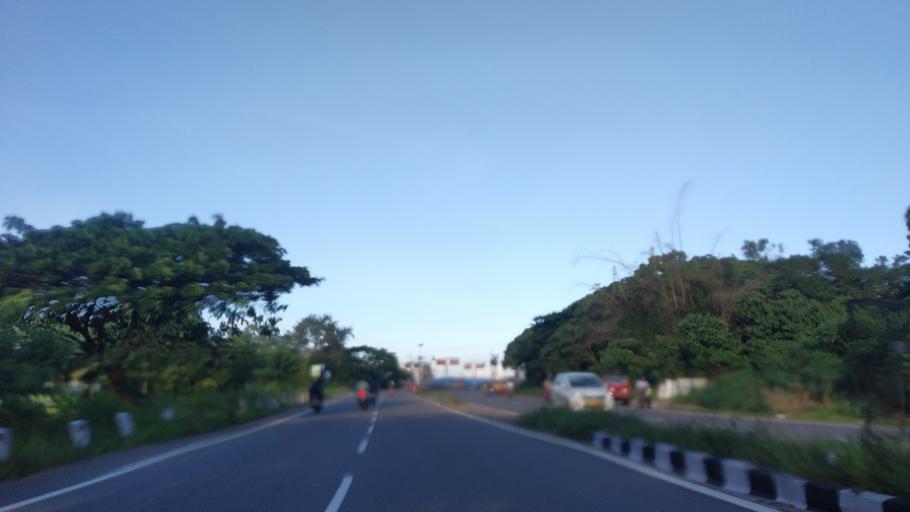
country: IN
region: Kerala
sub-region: Ernakulam
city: Elur
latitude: 10.0700
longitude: 76.3157
